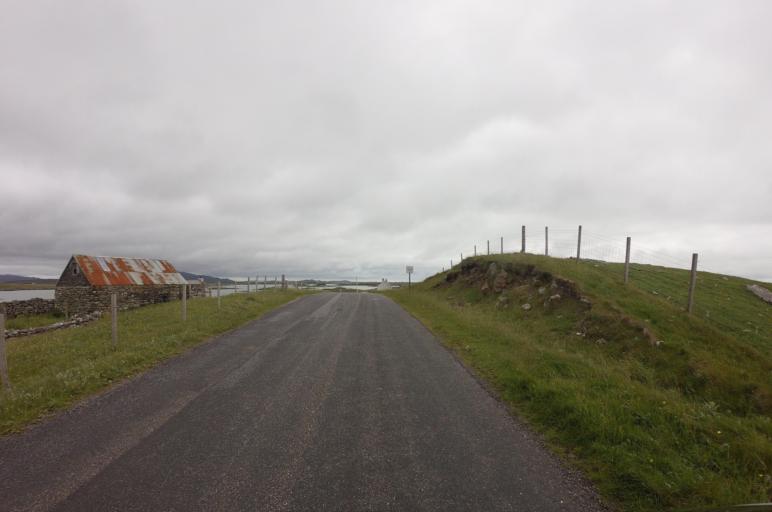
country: GB
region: Scotland
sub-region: Eilean Siar
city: Isle of North Uist
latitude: 57.5373
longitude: -7.3521
